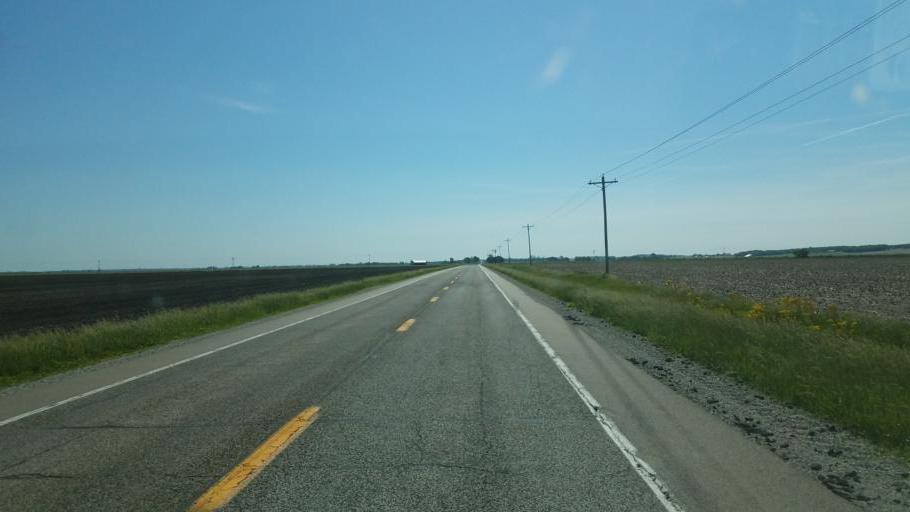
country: US
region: Illinois
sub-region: Mason County
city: Mason City
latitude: 40.3046
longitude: -89.7202
